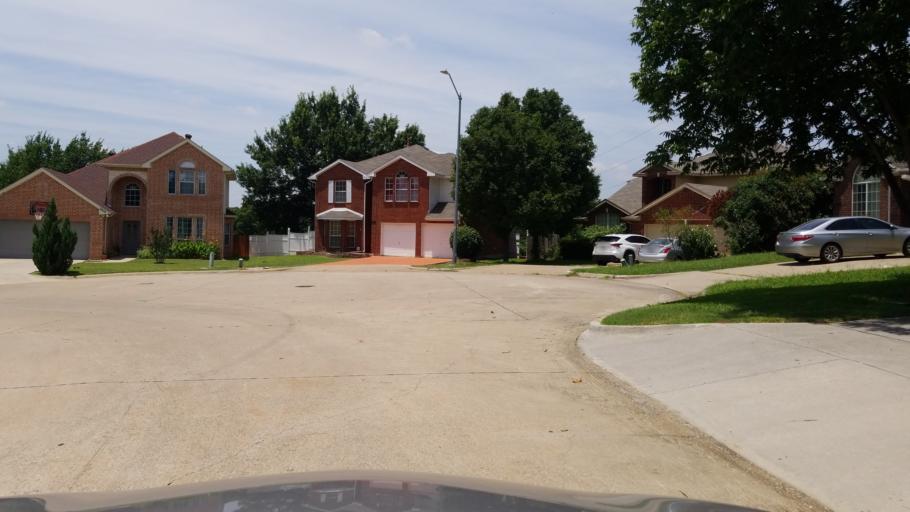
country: US
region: Texas
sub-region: Dallas County
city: Grand Prairie
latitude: 32.6806
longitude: -96.9909
